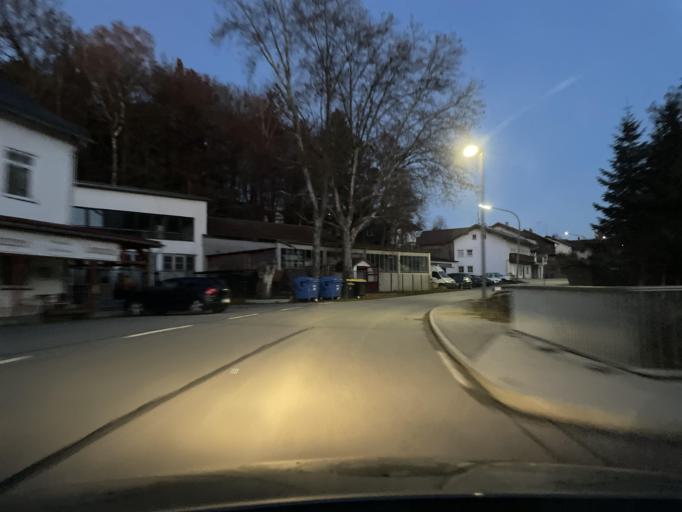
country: DE
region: Bavaria
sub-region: Lower Bavaria
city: Wittibreut
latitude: 48.3300
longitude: 12.9939
